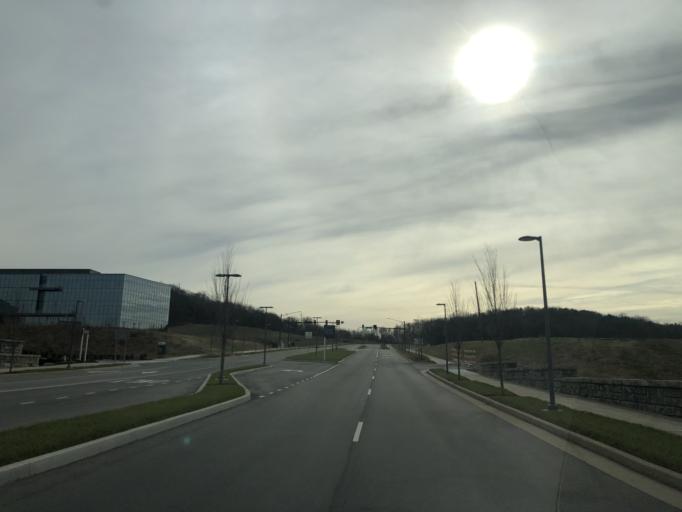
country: US
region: Tennessee
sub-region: Williamson County
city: Franklin
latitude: 35.9319
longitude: -86.8062
